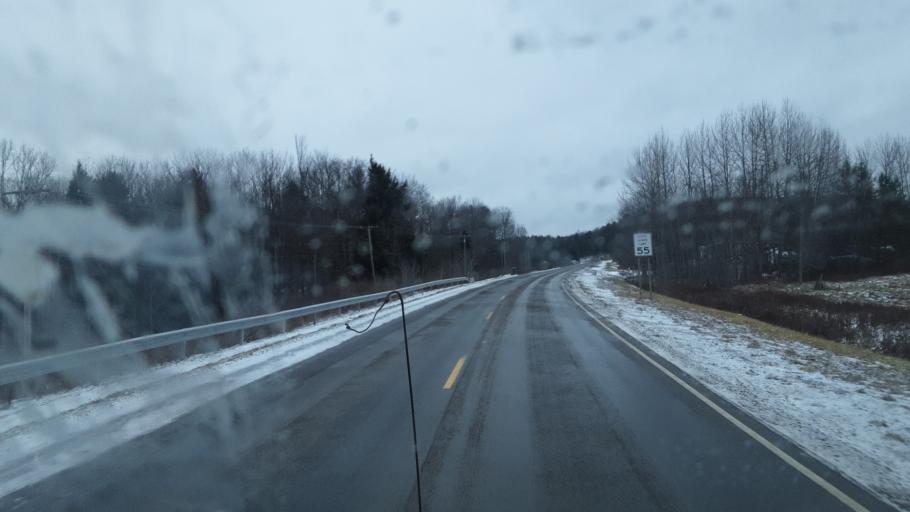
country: US
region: New York
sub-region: Allegany County
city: Friendship
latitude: 42.2162
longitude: -78.1448
